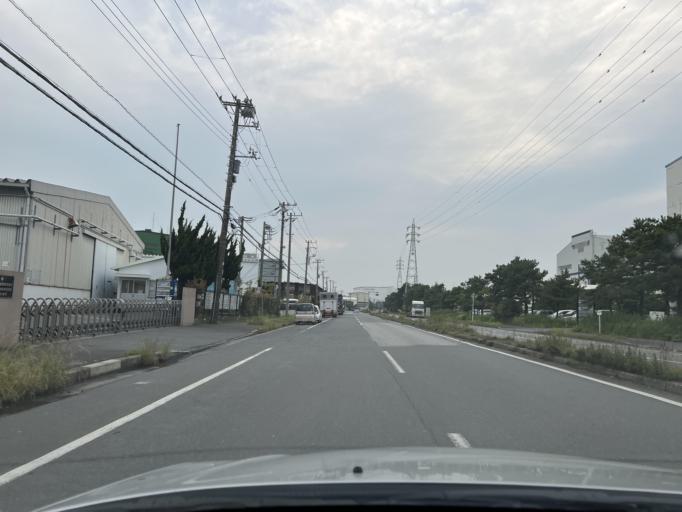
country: JP
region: Chiba
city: Funabashi
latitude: 35.6778
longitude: 139.9702
